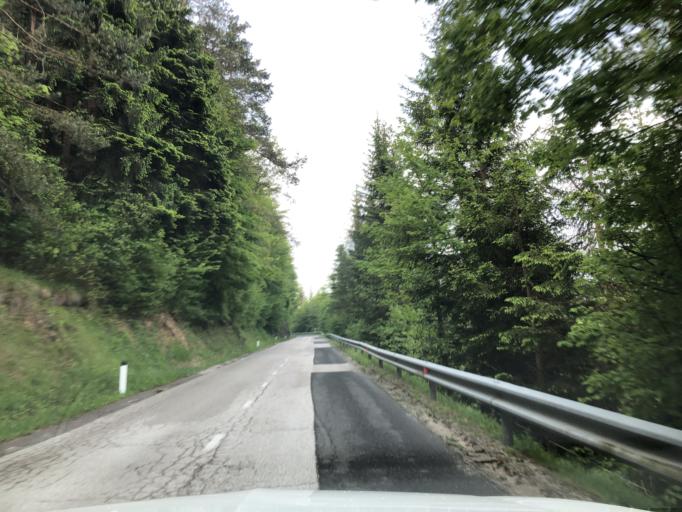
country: SI
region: Velike Lasce
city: Velike Lasce
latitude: 45.8194
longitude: 14.6268
